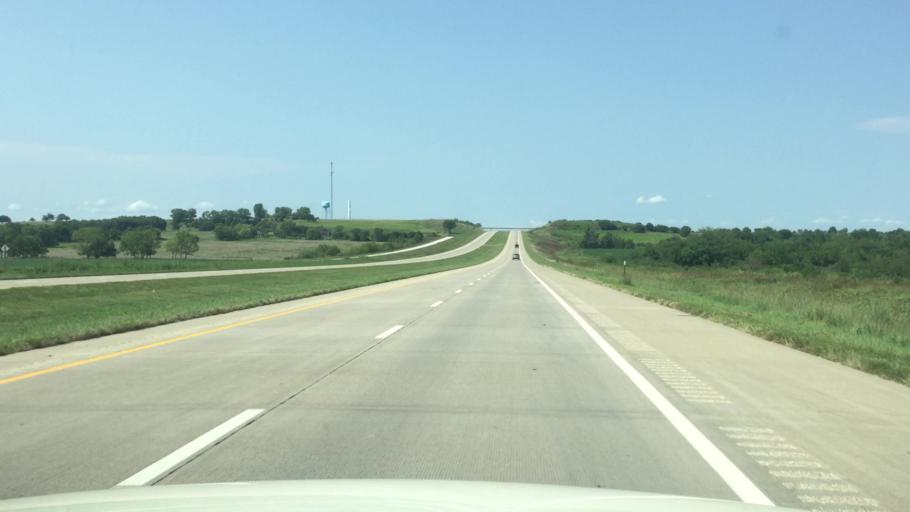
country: US
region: Kansas
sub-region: Linn County
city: Pleasanton
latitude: 38.0960
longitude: -94.7133
